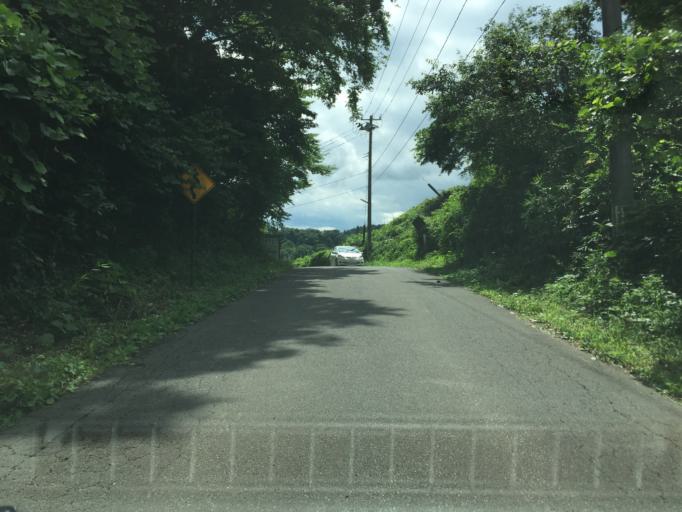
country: JP
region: Fukushima
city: Fukushima-shi
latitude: 37.7486
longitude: 140.5105
